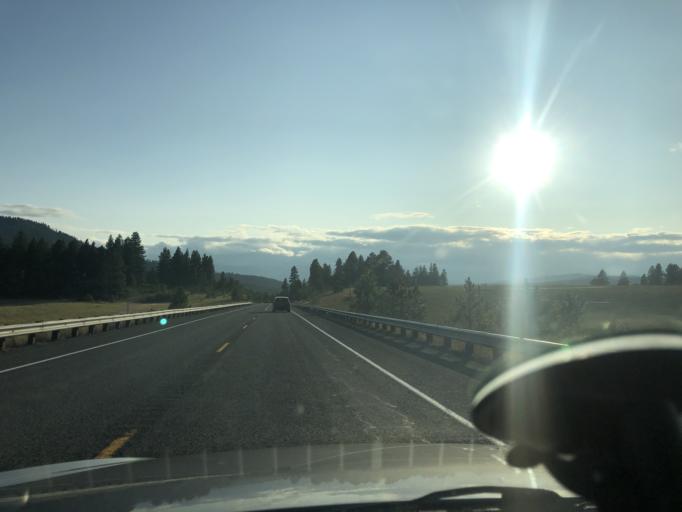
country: US
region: Washington
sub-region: Kittitas County
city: Cle Elum
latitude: 47.1986
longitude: -120.7432
